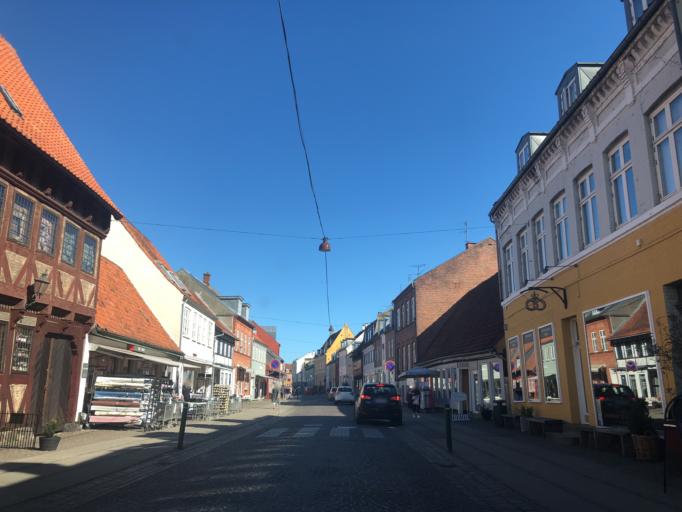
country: DK
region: Zealand
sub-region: Koge Kommune
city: Koge
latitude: 55.4572
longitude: 12.1787
